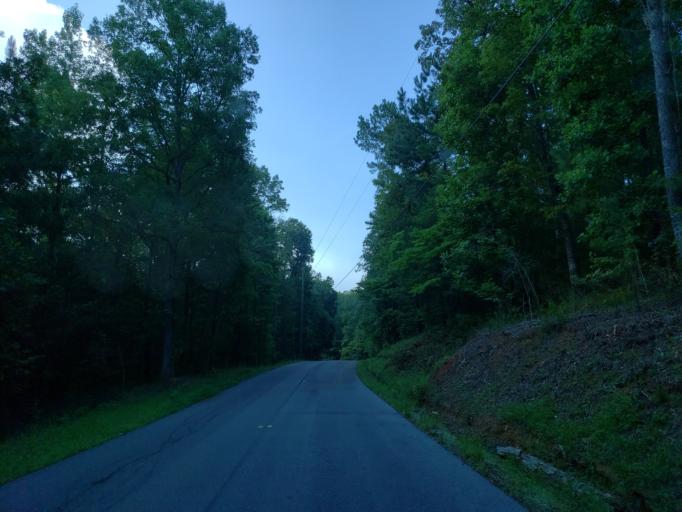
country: US
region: Georgia
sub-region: Paulding County
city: Dallas
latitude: 34.0136
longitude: -84.8988
